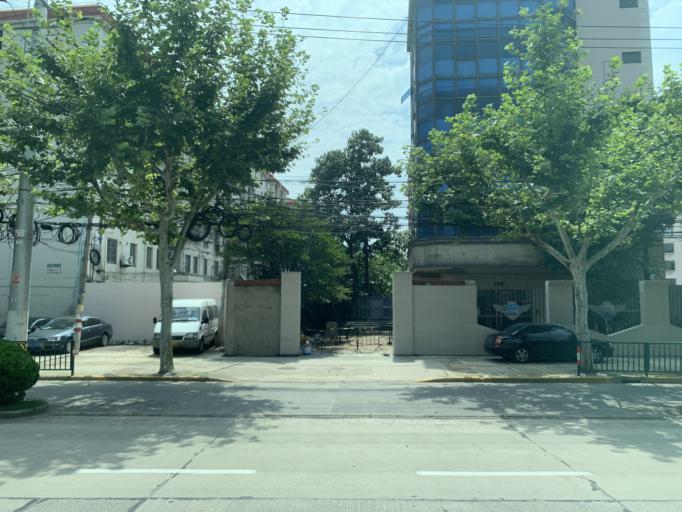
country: CN
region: Shanghai Shi
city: Pudong
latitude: 31.2391
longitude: 121.5272
